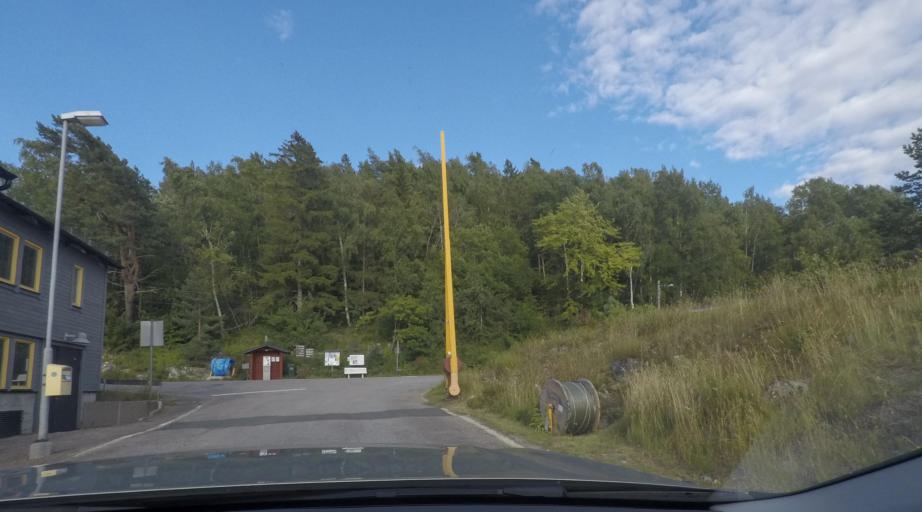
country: SE
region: Soedermanland
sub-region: Trosa Kommun
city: Trosa
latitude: 58.9716
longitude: 17.7119
